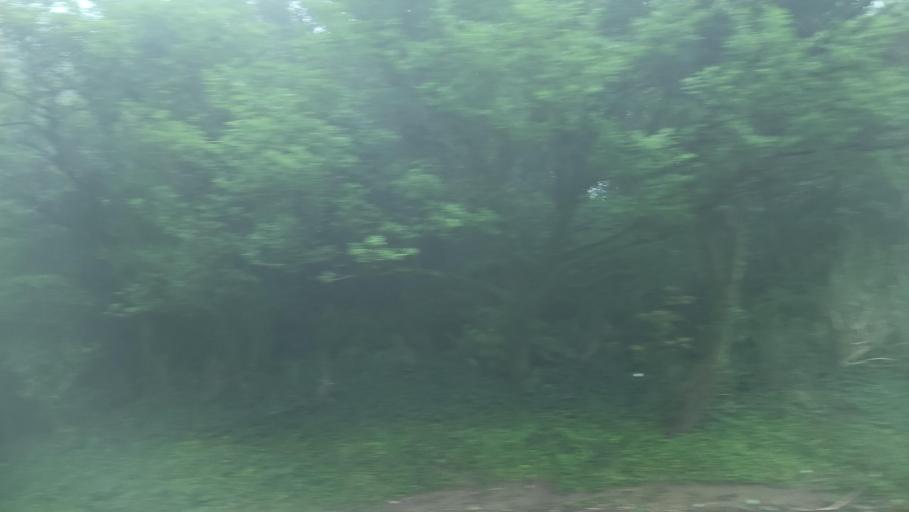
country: TW
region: Taipei
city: Taipei
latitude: 25.1380
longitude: 121.6032
